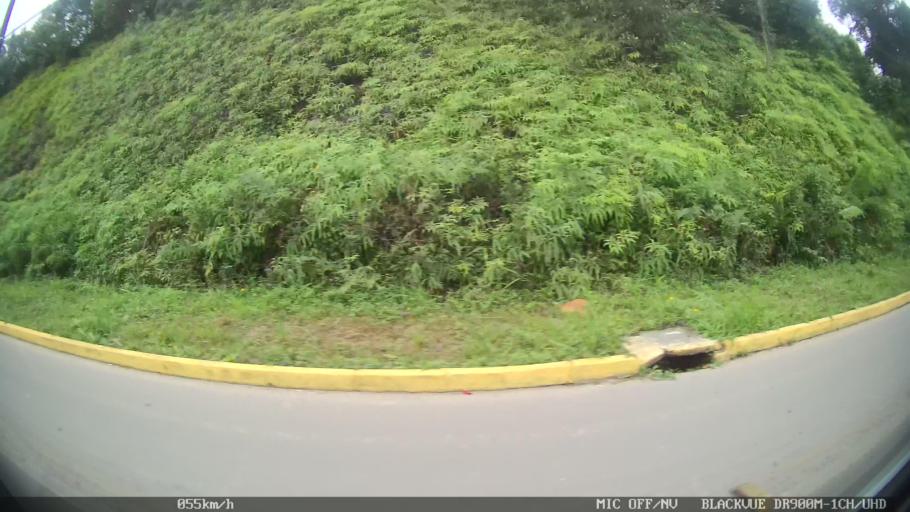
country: BR
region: Santa Catarina
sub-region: Joinville
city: Joinville
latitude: -26.3580
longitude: -48.8391
